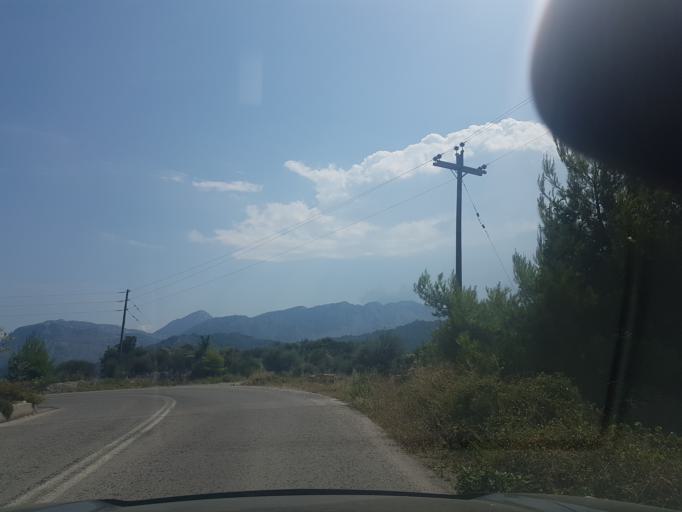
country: GR
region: Central Greece
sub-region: Nomos Evvoias
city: Kymi
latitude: 38.6496
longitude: 23.9108
